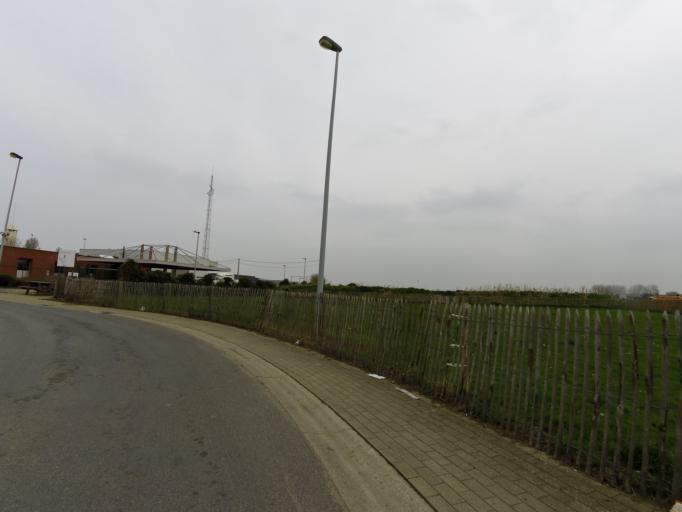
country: BE
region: Flanders
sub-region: Provincie West-Vlaanderen
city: Middelkerke
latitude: 51.1822
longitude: 2.8238
